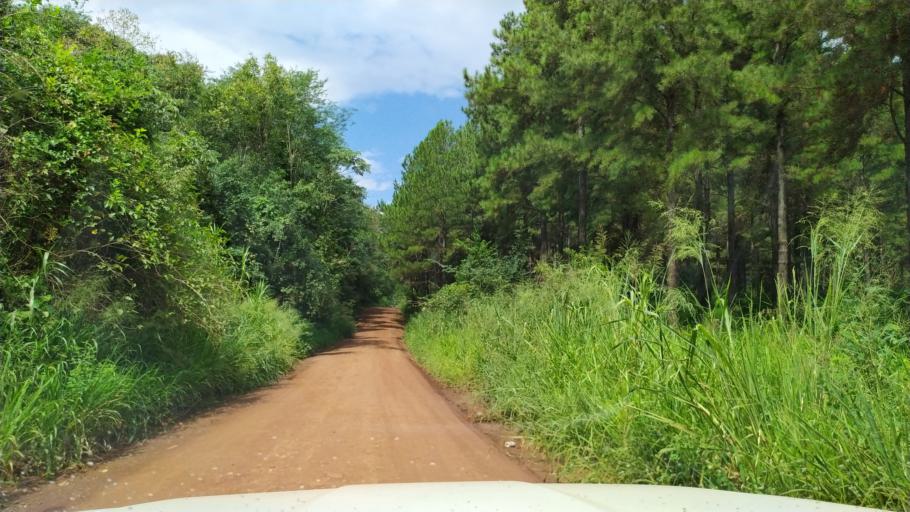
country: AR
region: Misiones
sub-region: Departamento de Eldorado
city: Eldorado
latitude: -26.4499
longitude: -54.6022
